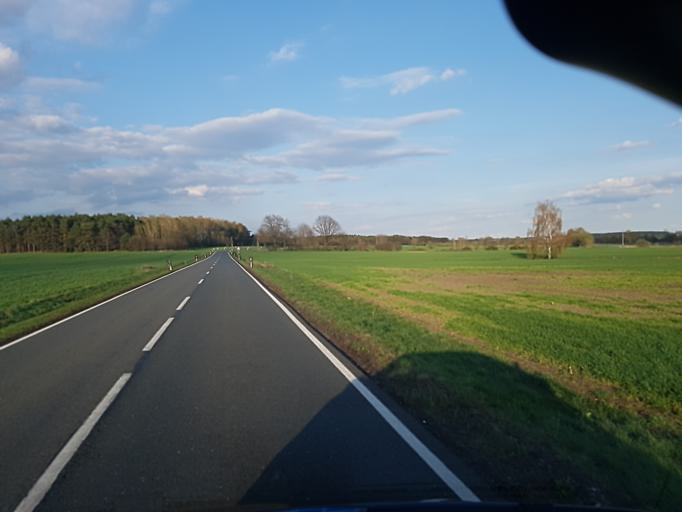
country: DE
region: Saxony
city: Lobnitz
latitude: 51.6219
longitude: 12.5137
